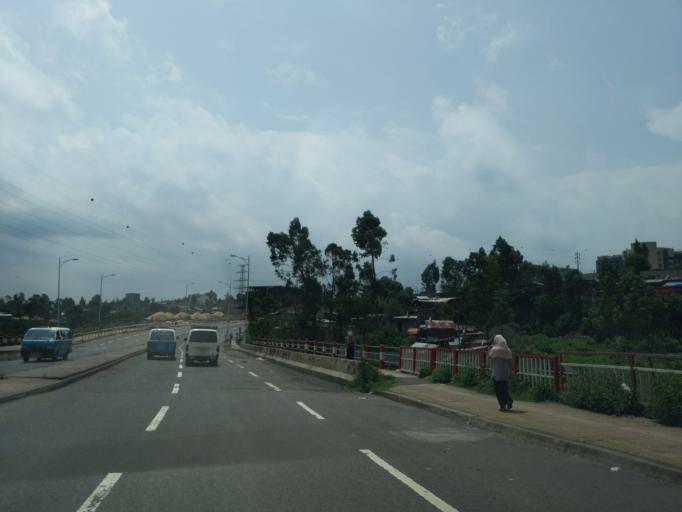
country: ET
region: Adis Abeba
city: Addis Ababa
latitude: 8.9494
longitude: 38.7594
